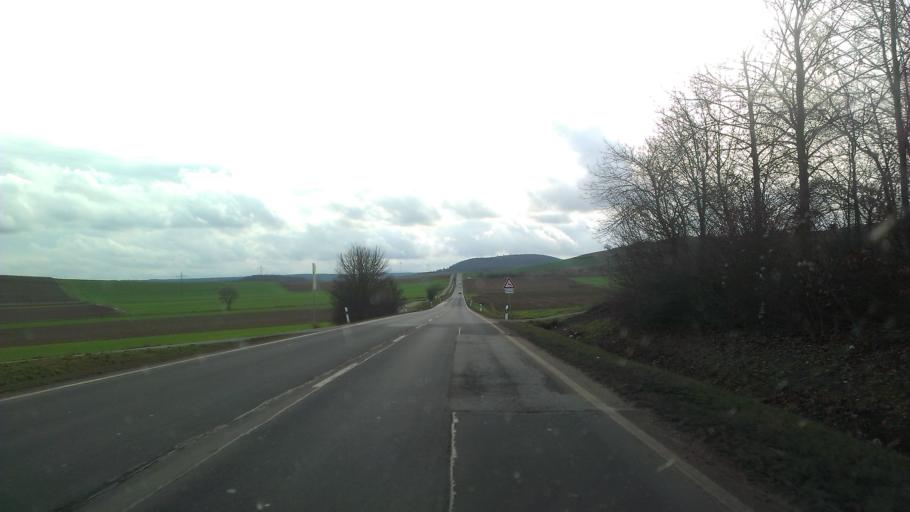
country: DE
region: Rheinland-Pfalz
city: Hackenheim
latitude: 49.8198
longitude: 7.9066
